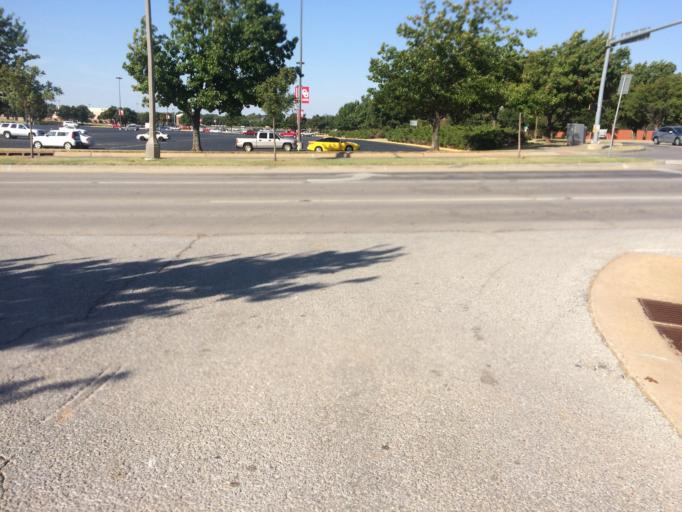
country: US
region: Oklahoma
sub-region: Cleveland County
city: Norman
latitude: 35.1893
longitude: -97.4411
